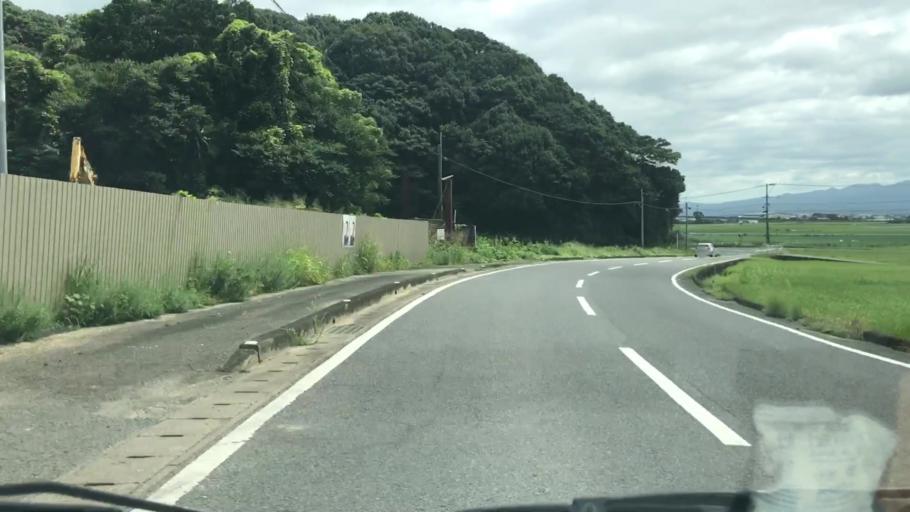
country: JP
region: Saga Prefecture
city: Takeocho-takeo
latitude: 33.2317
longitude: 130.1519
